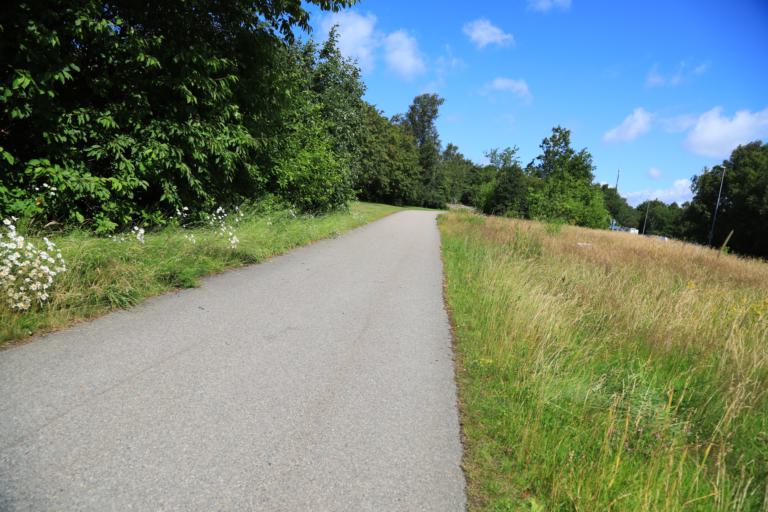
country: SE
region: Halland
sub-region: Varbergs Kommun
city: Traslovslage
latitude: 57.0995
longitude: 12.2946
